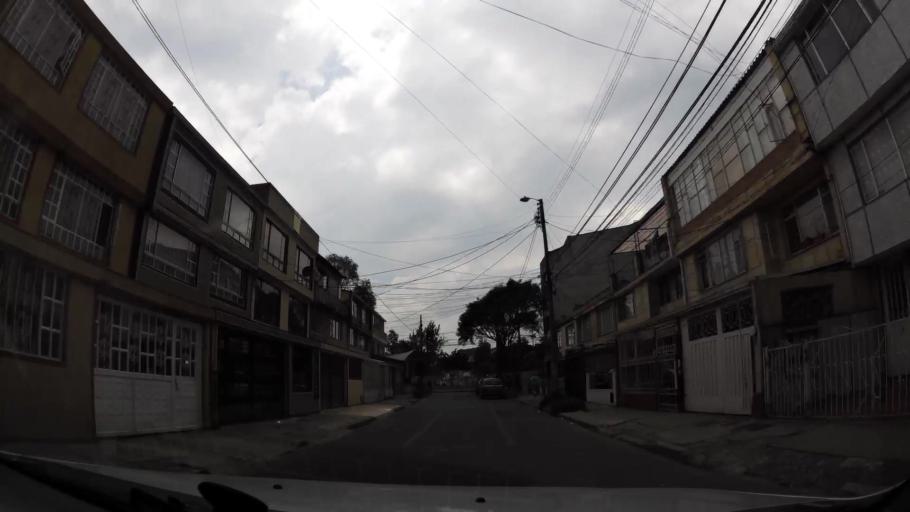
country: CO
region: Bogota D.C.
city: Bogota
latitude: 4.6191
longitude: -74.1121
